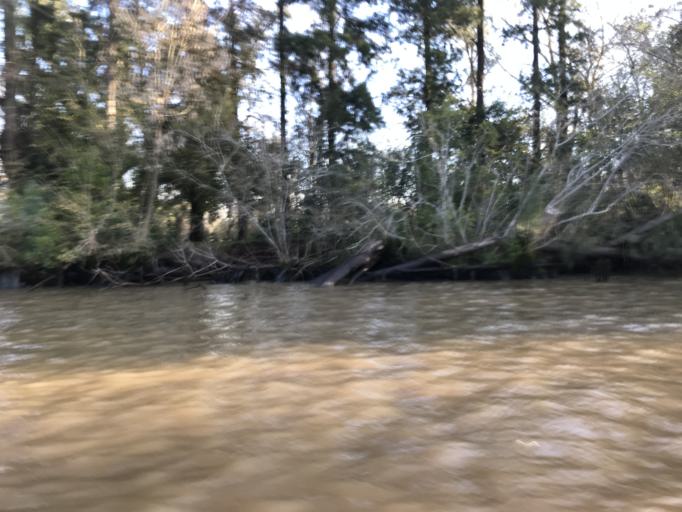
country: AR
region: Buenos Aires
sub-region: Partido de Tigre
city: Tigre
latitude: -34.3737
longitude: -58.5801
